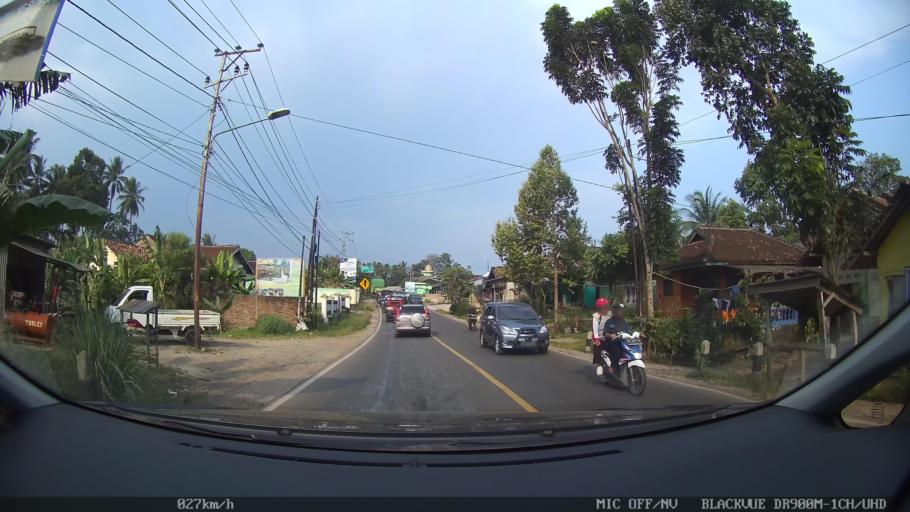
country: ID
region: Lampung
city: Natar
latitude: -5.3643
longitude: 105.1844
